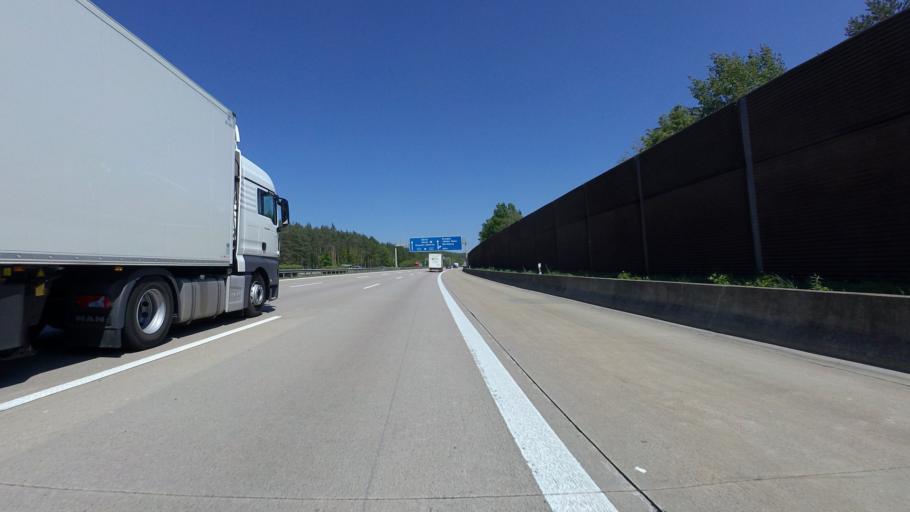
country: DE
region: Saxony
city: Radebeul
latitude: 51.0985
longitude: 13.7042
